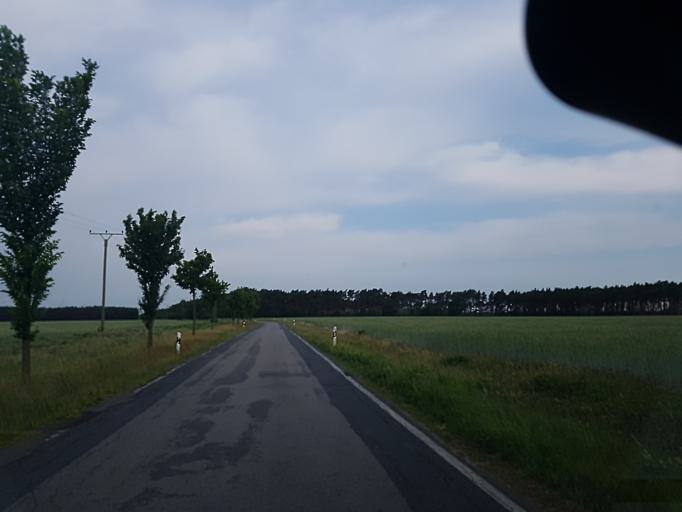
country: DE
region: Saxony-Anhalt
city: Seyda
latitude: 51.8430
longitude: 12.9208
